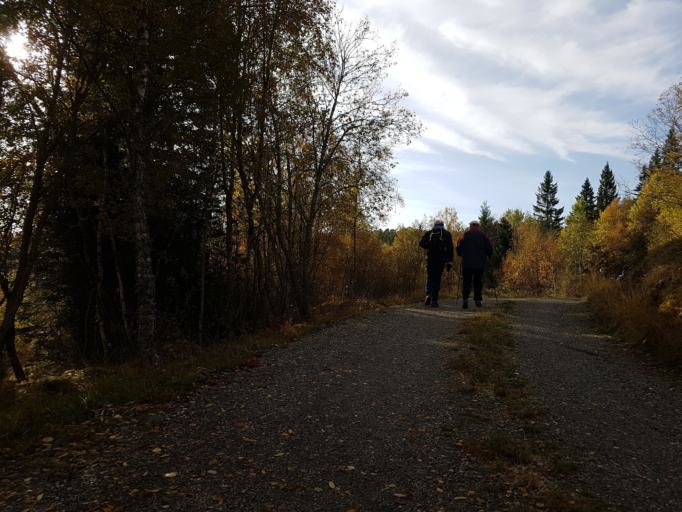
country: NO
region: Sor-Trondelag
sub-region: Trondheim
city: Trondheim
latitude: 63.4478
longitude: 10.2833
